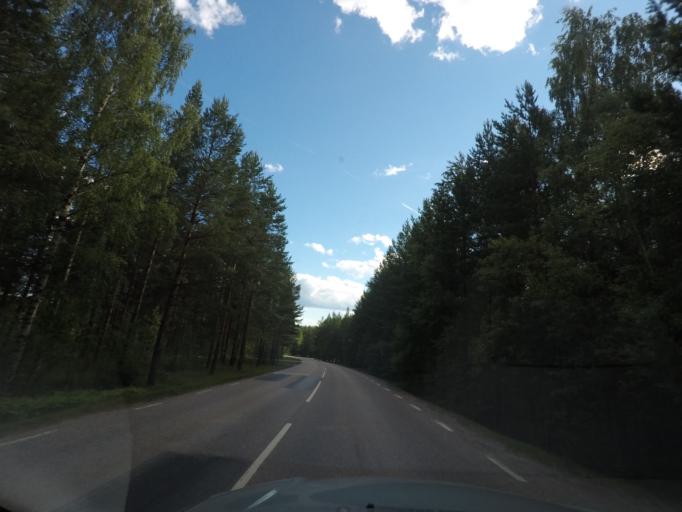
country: SE
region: Stockholm
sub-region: Sigtuna Kommun
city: Rosersberg
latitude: 59.6602
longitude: 17.9781
